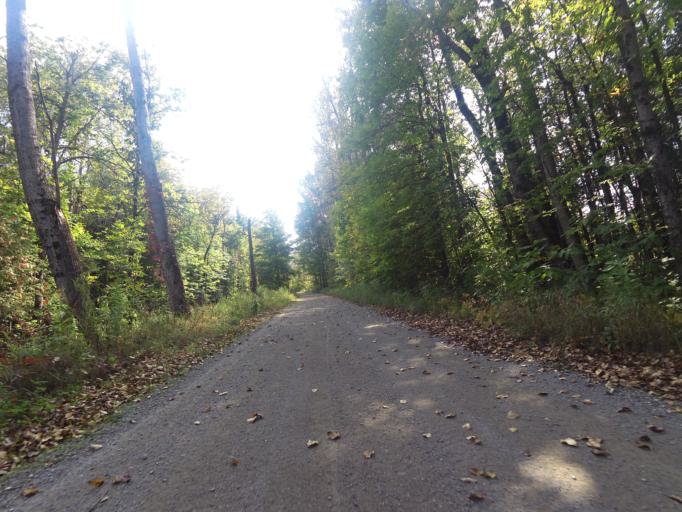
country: CA
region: Ontario
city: Renfrew
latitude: 45.1554
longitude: -76.6878
